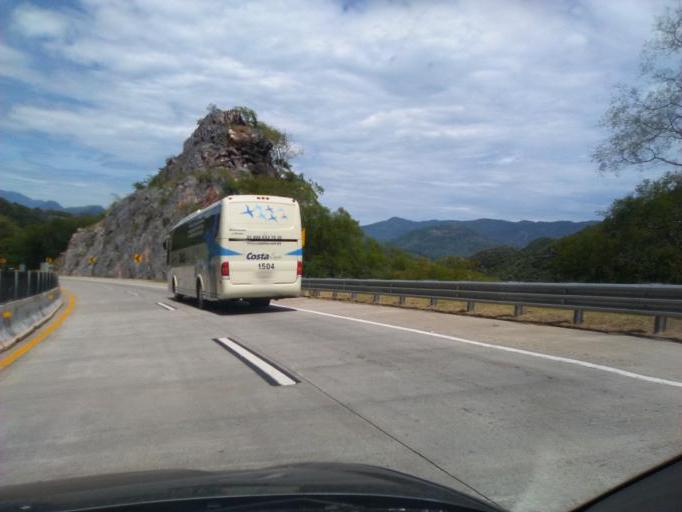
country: MX
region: Guerrero
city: Tierra Colorada
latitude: 17.1171
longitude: -99.5678
